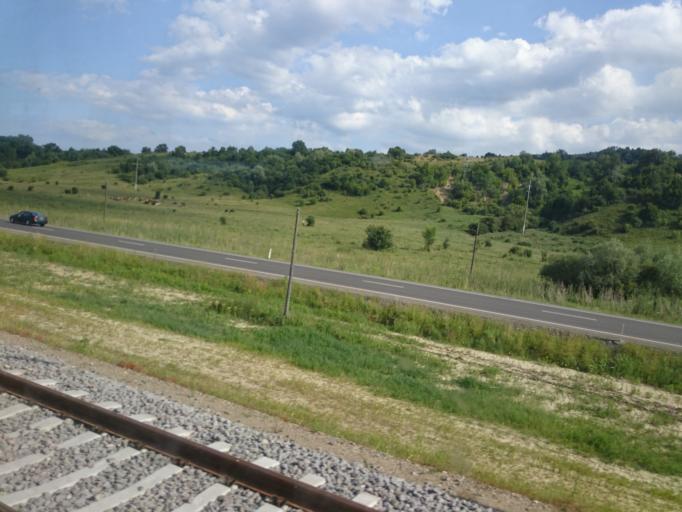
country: RO
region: Sibiu
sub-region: Comuna Hoghilag
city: Hoghilag
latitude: 46.2201
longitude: 24.6131
